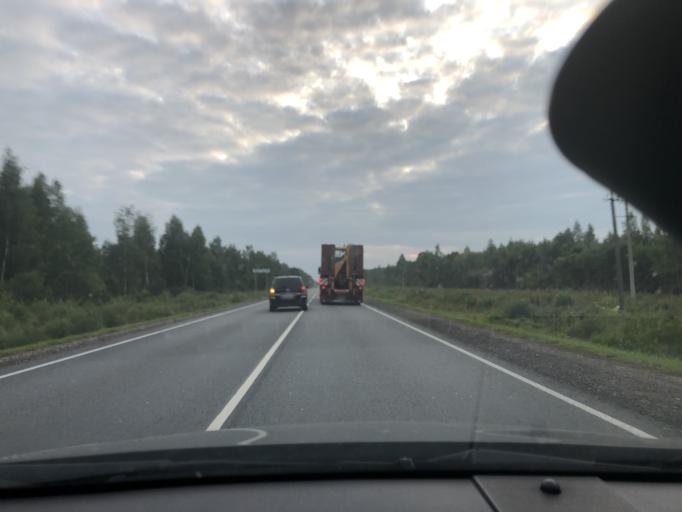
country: RU
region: Kaluga
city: Ferzikovo
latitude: 54.3588
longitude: 36.7648
